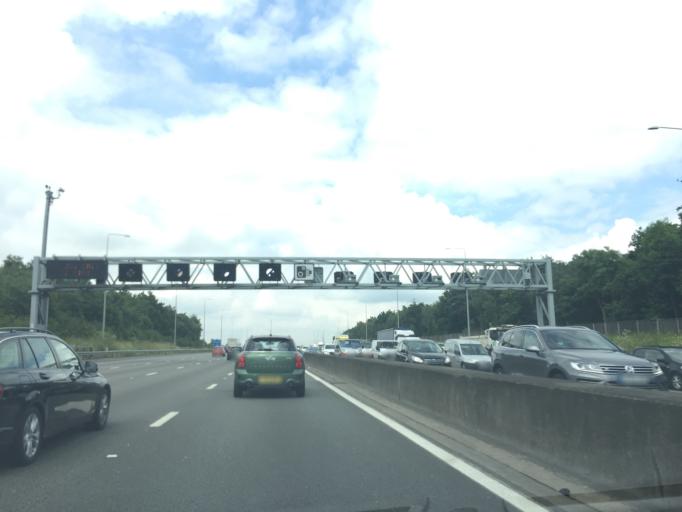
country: GB
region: England
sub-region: Buckinghamshire
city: Gerrards Cross
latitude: 51.5933
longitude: -0.5327
